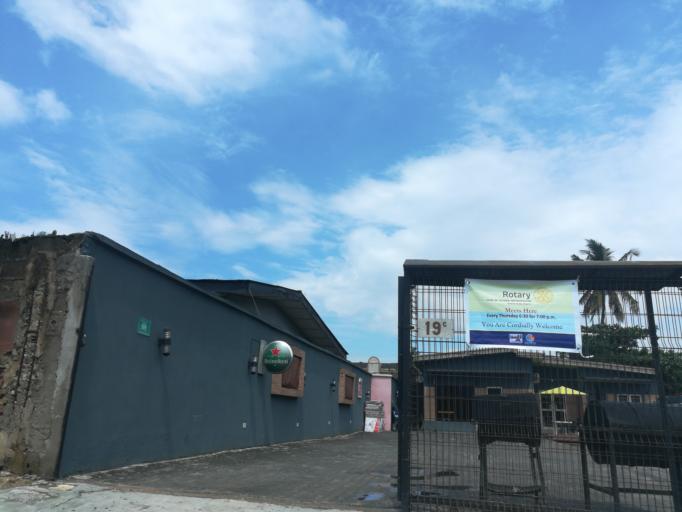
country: NG
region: Lagos
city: Somolu
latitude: 6.5612
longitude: 3.3681
